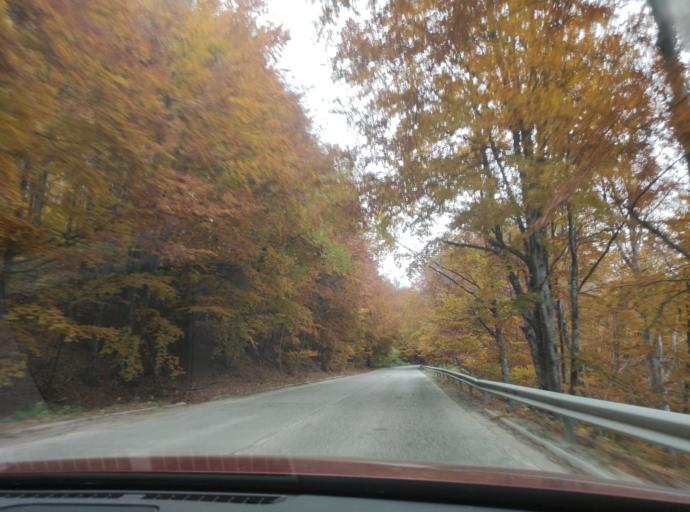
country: BG
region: Montana
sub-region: Obshtina Berkovitsa
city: Berkovitsa
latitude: 43.1164
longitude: 23.1138
